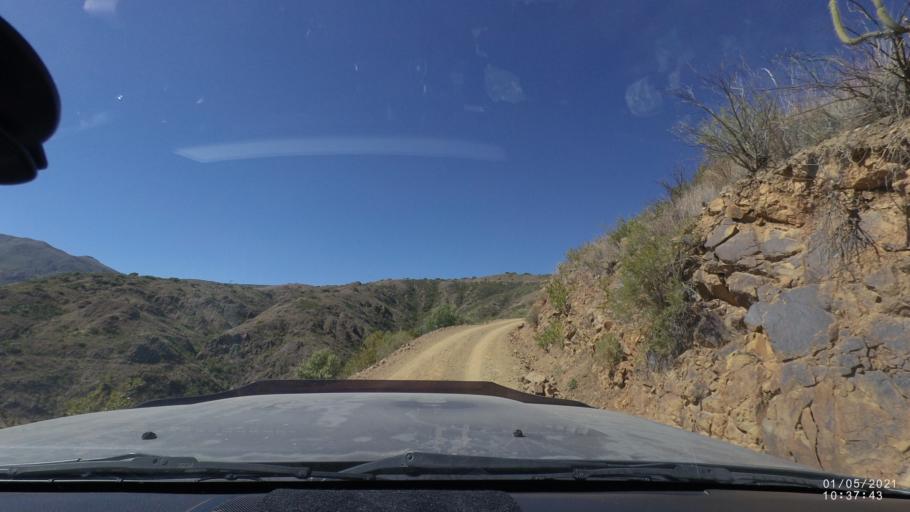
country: BO
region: Cochabamba
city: Capinota
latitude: -17.6019
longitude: -66.1855
